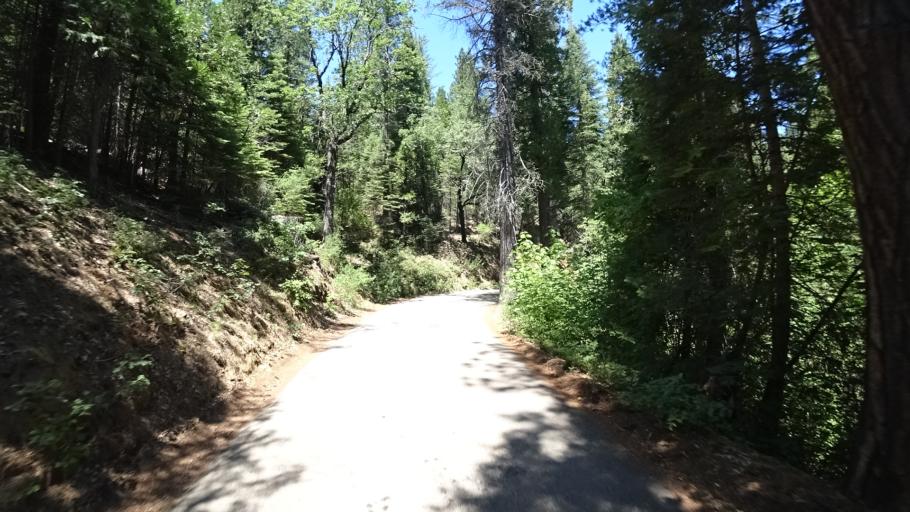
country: US
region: California
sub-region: Calaveras County
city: Arnold
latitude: 38.2223
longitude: -120.3590
